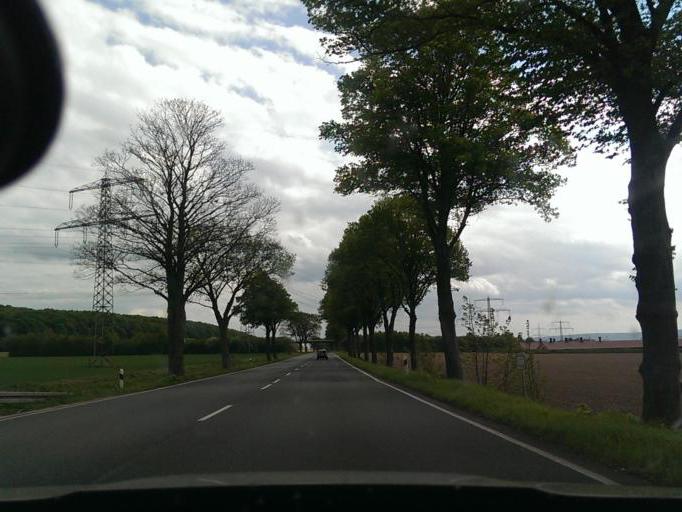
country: DE
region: Lower Saxony
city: Nordstemmen
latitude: 52.1814
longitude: 9.7461
